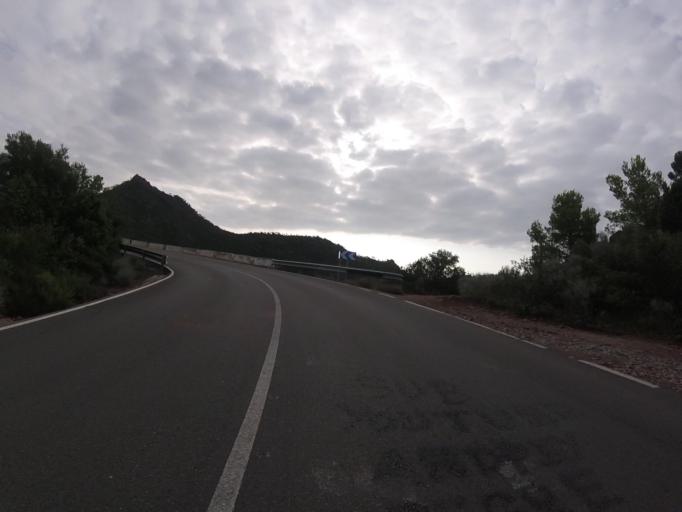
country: ES
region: Valencia
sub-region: Provincia de Castello
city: Benicassim
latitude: 40.0716
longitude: 0.0444
